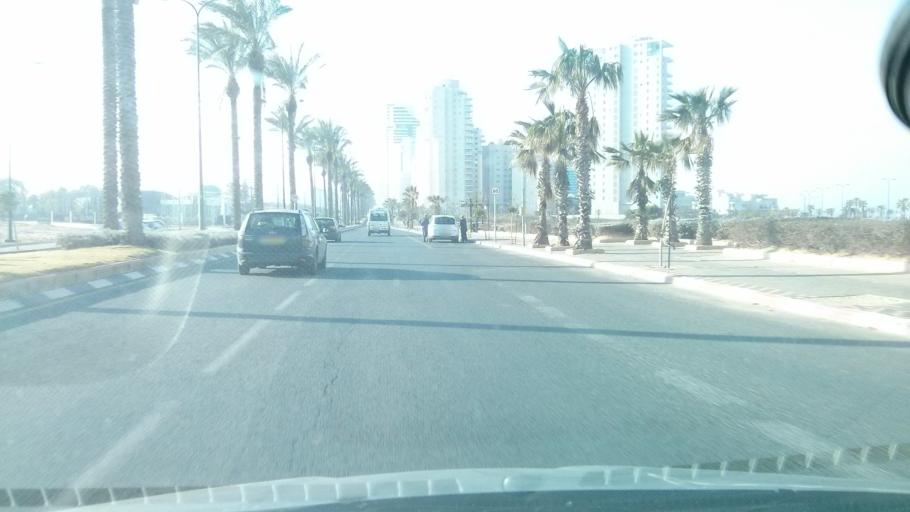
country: IL
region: Central District
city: Netanya
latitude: 32.3133
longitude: 34.8479
